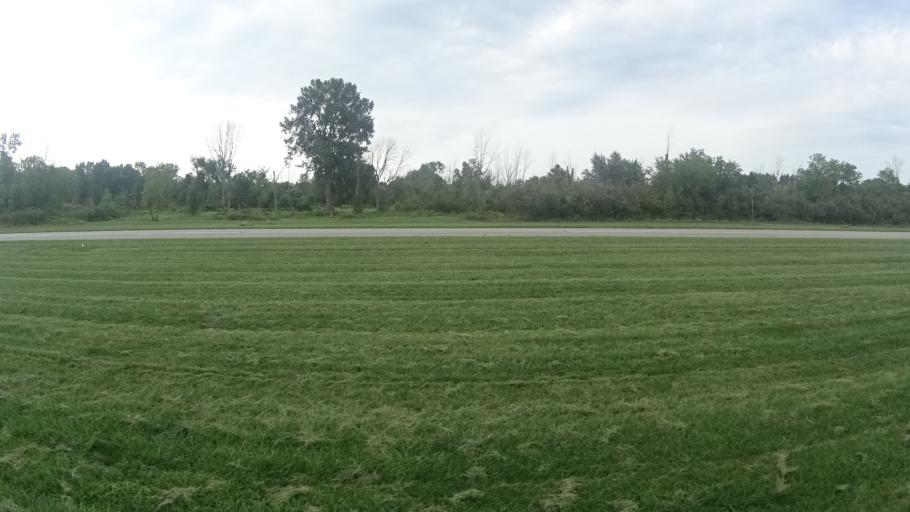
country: US
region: Ohio
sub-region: Erie County
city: Sandusky
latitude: 41.6035
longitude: -82.6819
